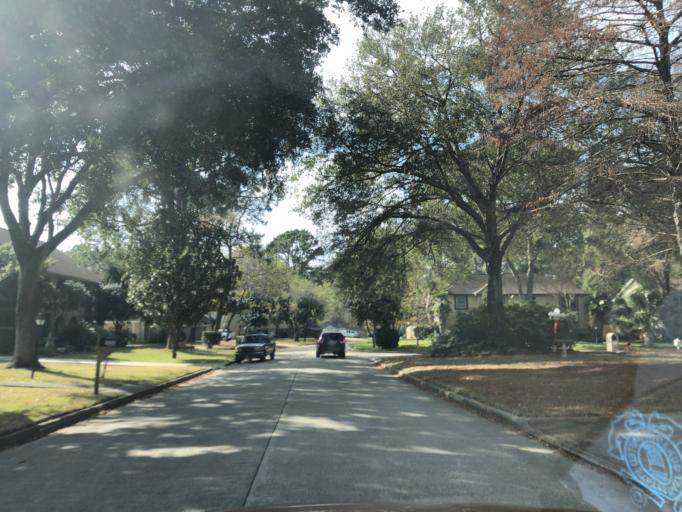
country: US
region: Texas
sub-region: Harris County
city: Tomball
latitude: 30.0257
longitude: -95.5453
